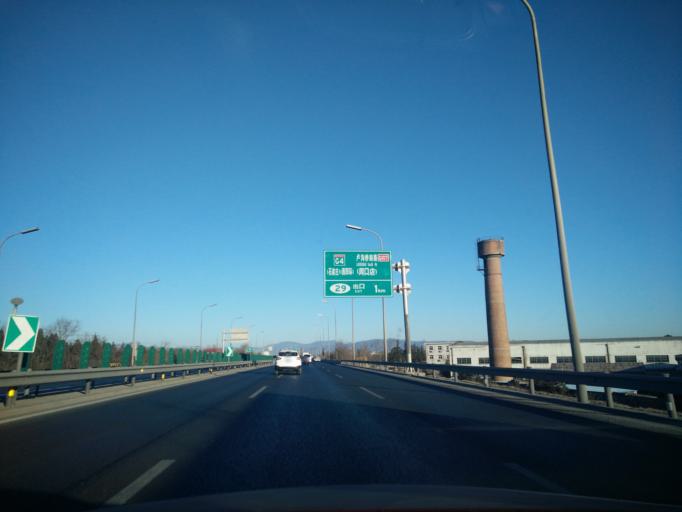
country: CN
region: Beijing
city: Fengtai
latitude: 39.8344
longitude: 116.2285
